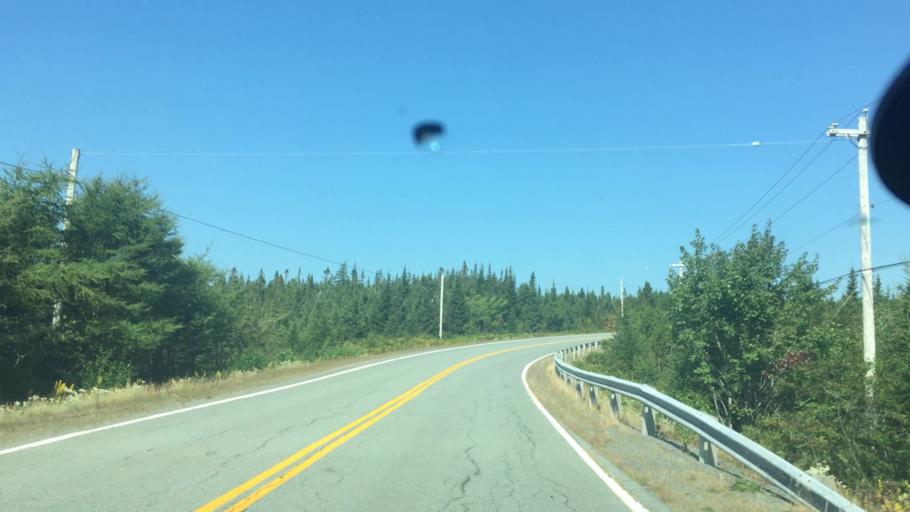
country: CA
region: Nova Scotia
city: Antigonish
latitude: 45.0074
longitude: -62.1053
